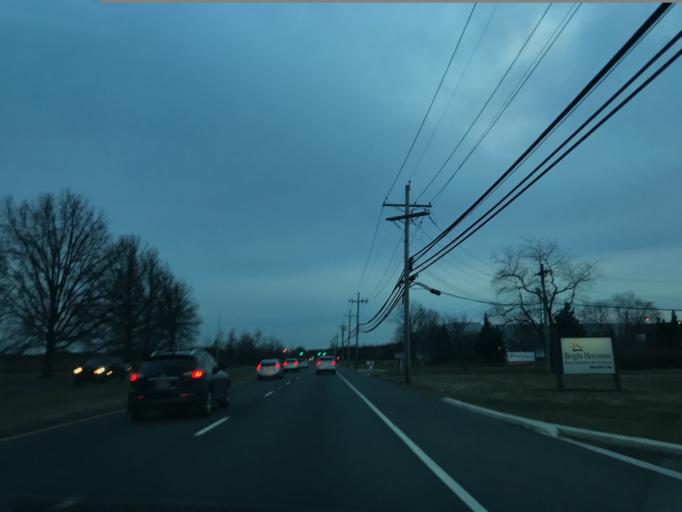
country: US
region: New Jersey
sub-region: Middlesex County
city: Rossmoor
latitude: 40.3412
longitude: -74.5008
